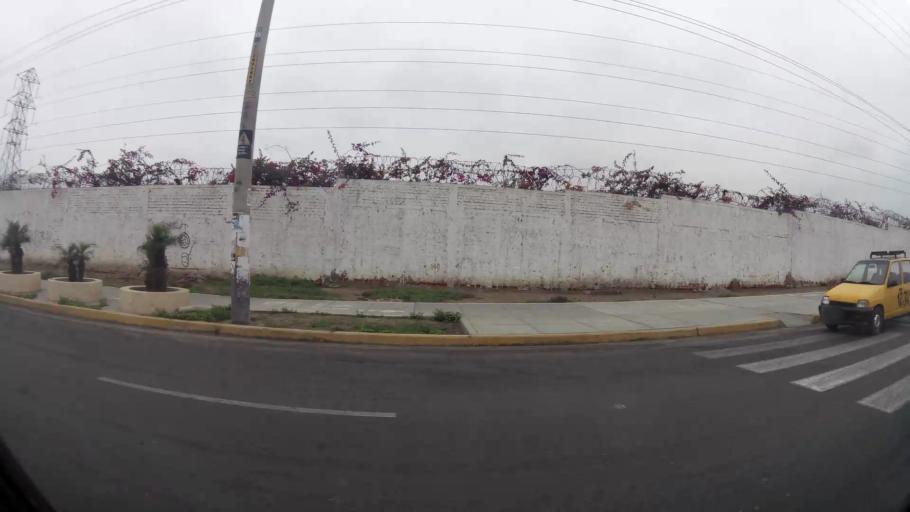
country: PE
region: Ancash
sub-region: Provincia de Santa
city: Chimbote
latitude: -9.0639
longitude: -78.5904
